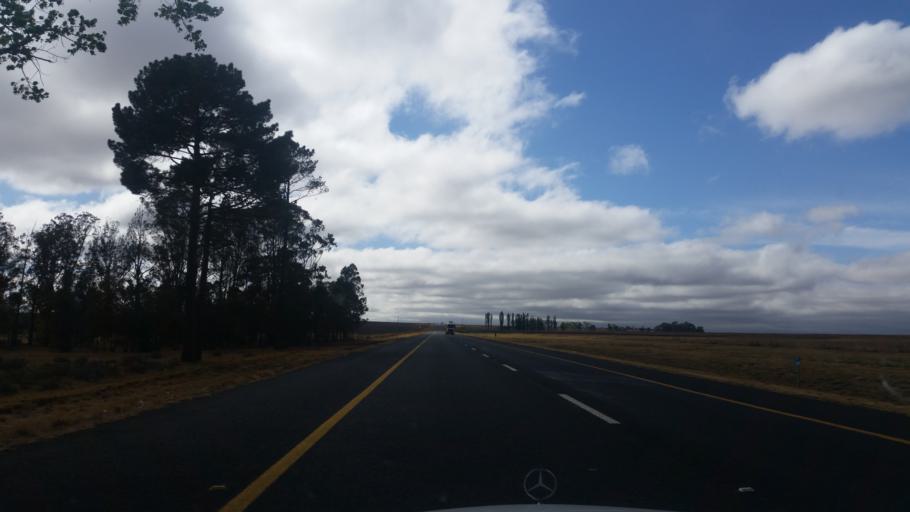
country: ZA
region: Orange Free State
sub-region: Thabo Mofutsanyana District Municipality
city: Harrismith
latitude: -28.2707
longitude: 28.8849
